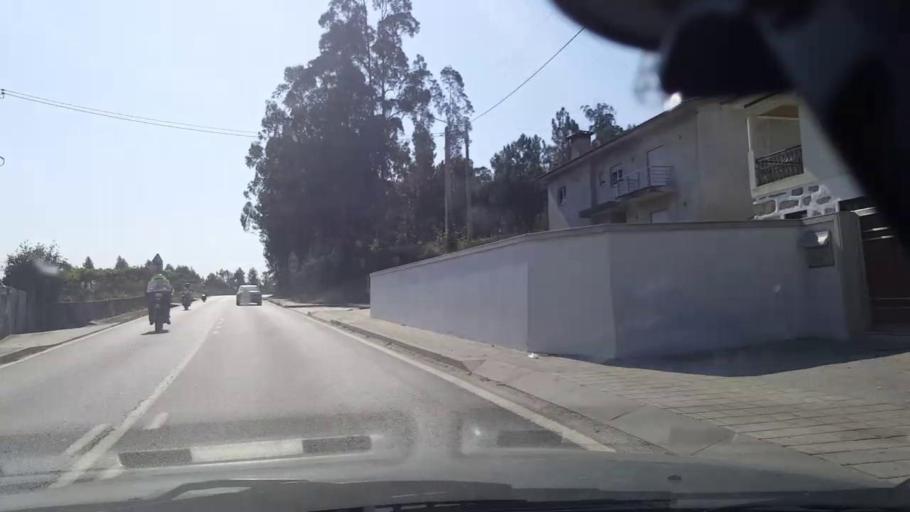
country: PT
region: Porto
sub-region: Povoa de Varzim
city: Pedroso
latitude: 41.4105
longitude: -8.6684
